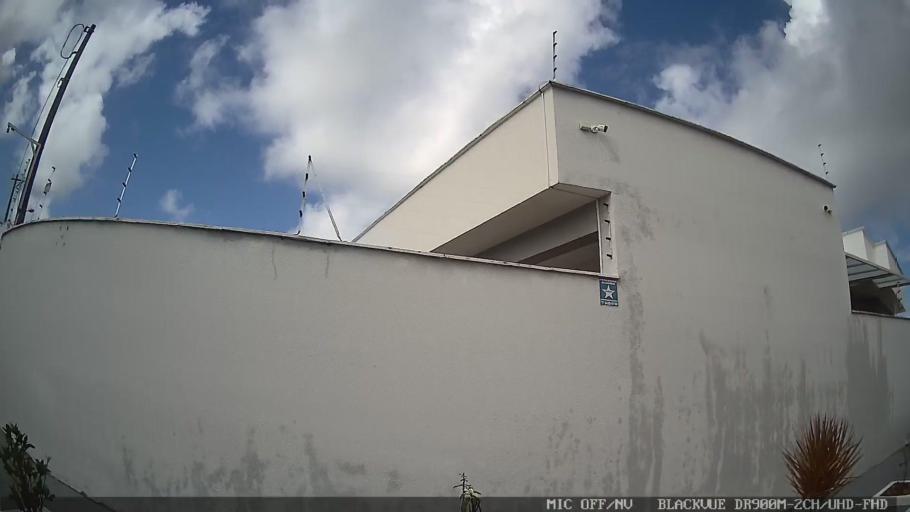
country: BR
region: Sao Paulo
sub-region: Itanhaem
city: Itanhaem
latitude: -24.2322
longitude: -46.8720
